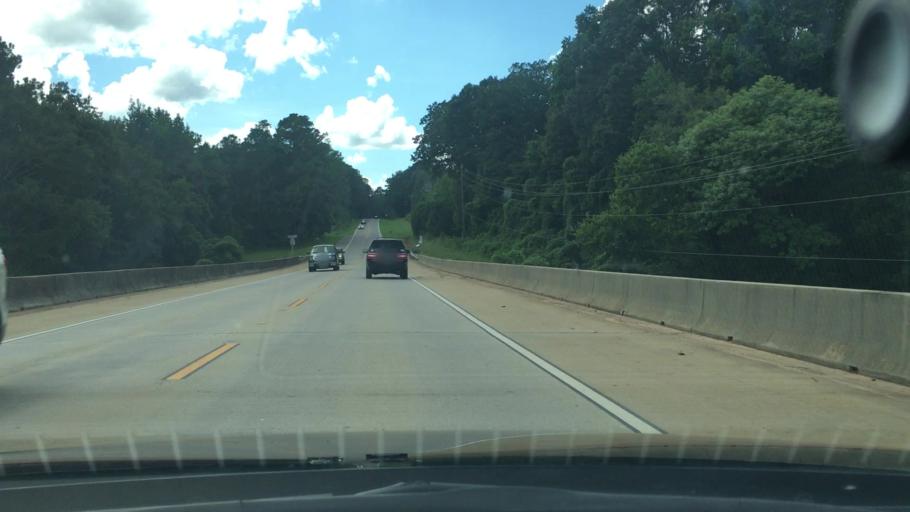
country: US
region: Georgia
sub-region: Putnam County
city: Eatonton
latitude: 33.3141
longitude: -83.4366
